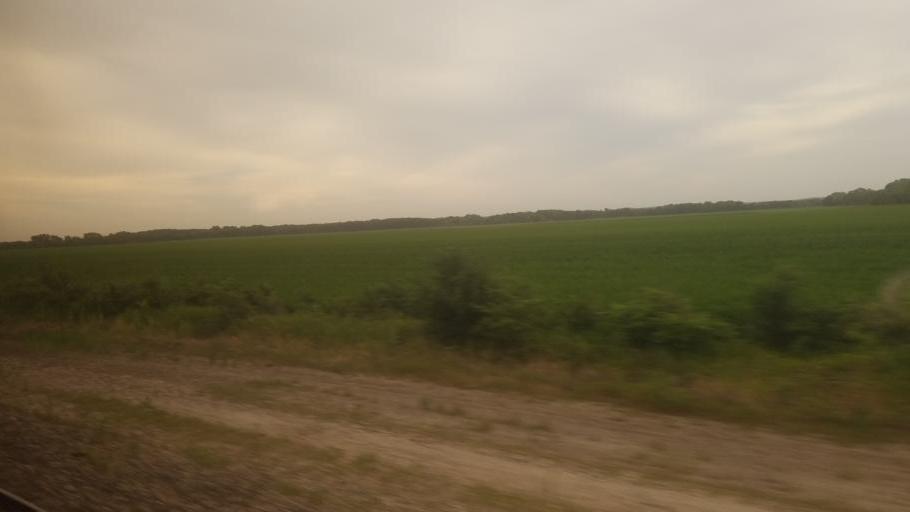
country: US
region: Kansas
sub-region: Chase County
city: Cottonwood Falls
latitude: 38.3915
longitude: -96.5309
